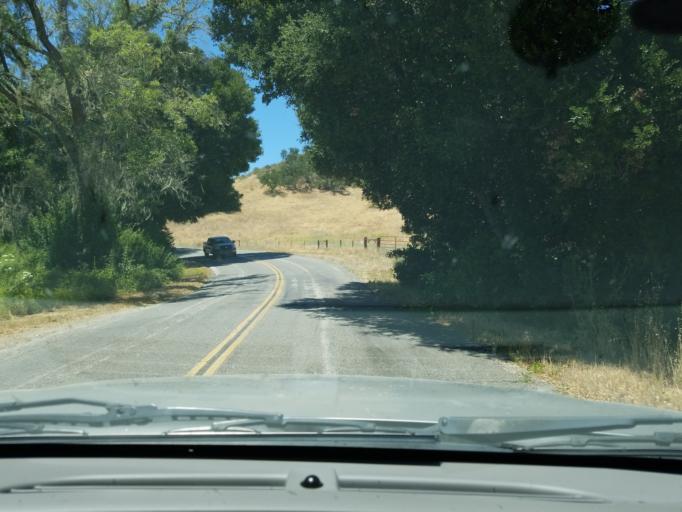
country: US
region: California
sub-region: Monterey County
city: Carmel Valley Village
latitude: 36.4428
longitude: -121.6497
